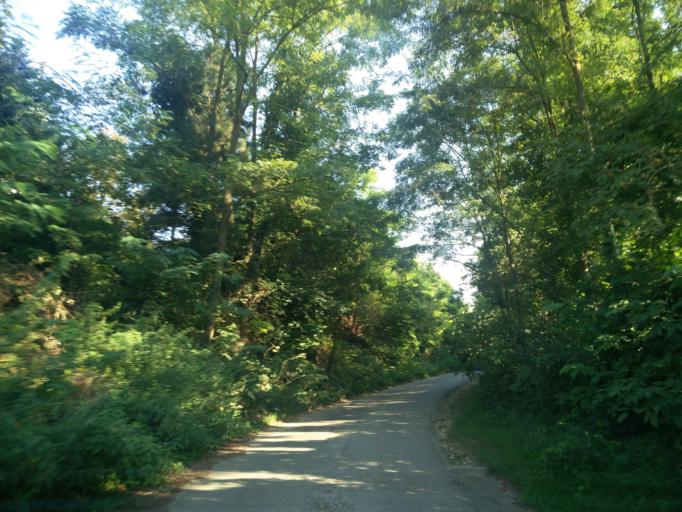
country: HU
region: Zala
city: Zalaegerszeg
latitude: 46.8302
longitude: 16.8794
